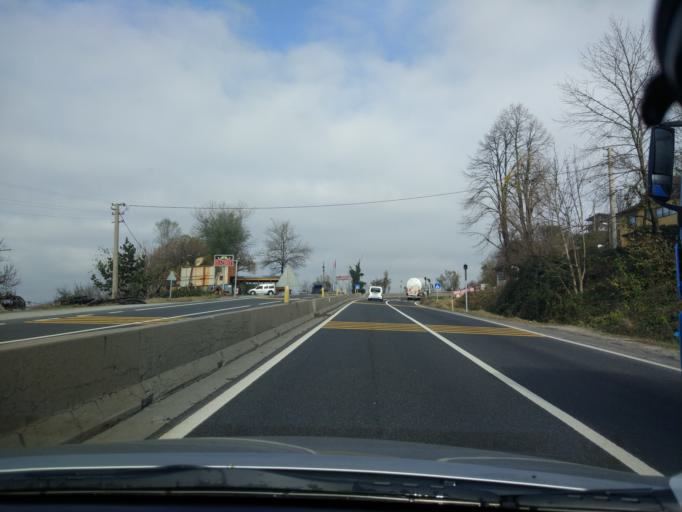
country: TR
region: Duzce
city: Kaynasli
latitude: 40.7499
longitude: 31.3834
